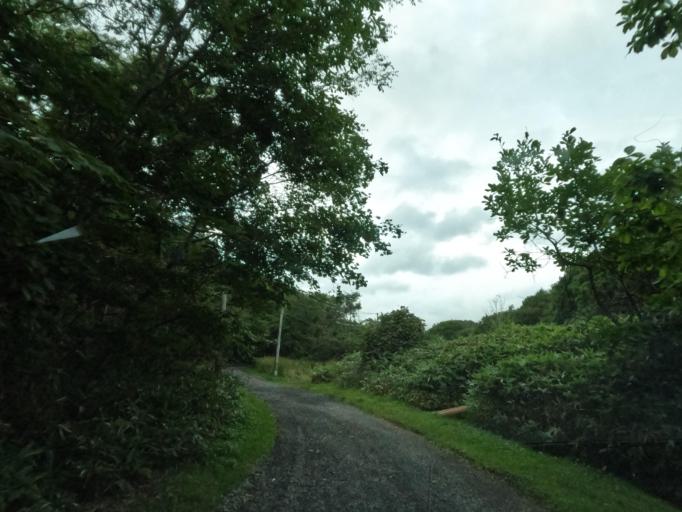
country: JP
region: Hokkaido
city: Muroran
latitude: 42.3696
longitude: 140.9667
